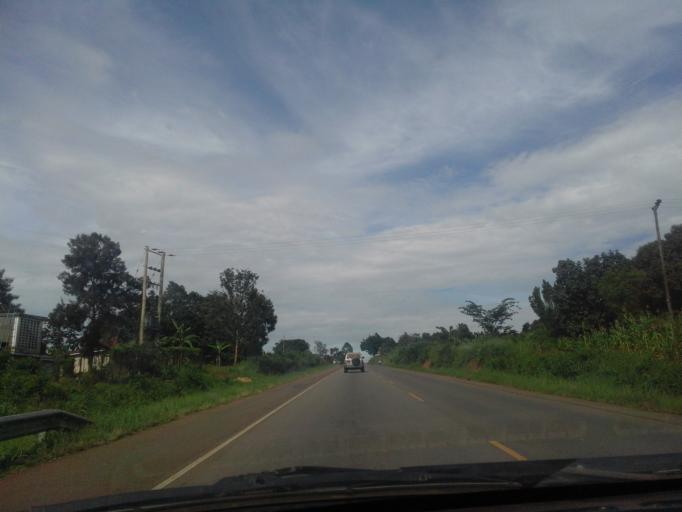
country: UG
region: Central Region
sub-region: Lwengo District
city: Lwengo
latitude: -0.3589
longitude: 31.5447
